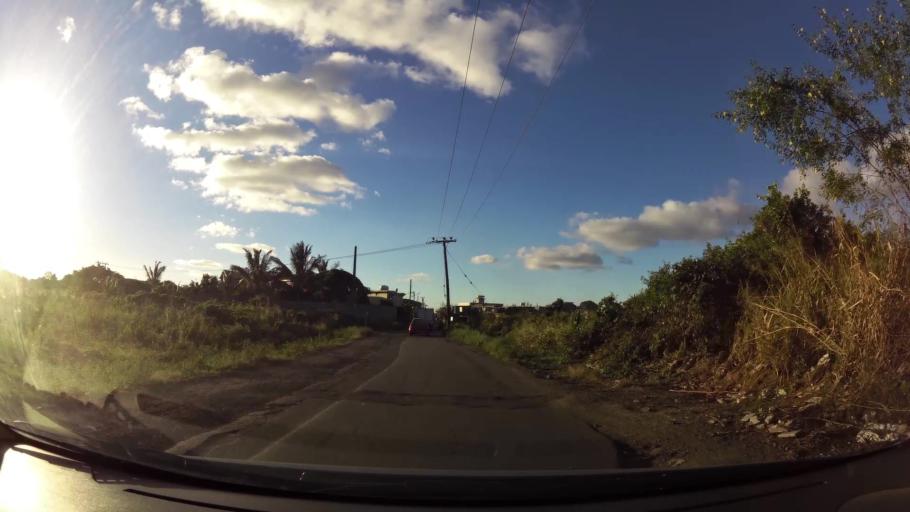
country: MU
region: Plaines Wilhems
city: Quatre Bornes
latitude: -20.2563
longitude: 57.4617
